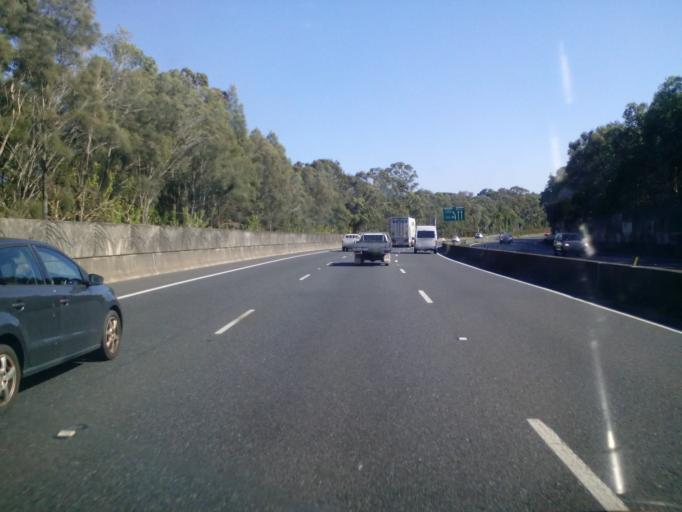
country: AU
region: New South Wales
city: Chinderah
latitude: -28.2390
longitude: 153.5622
